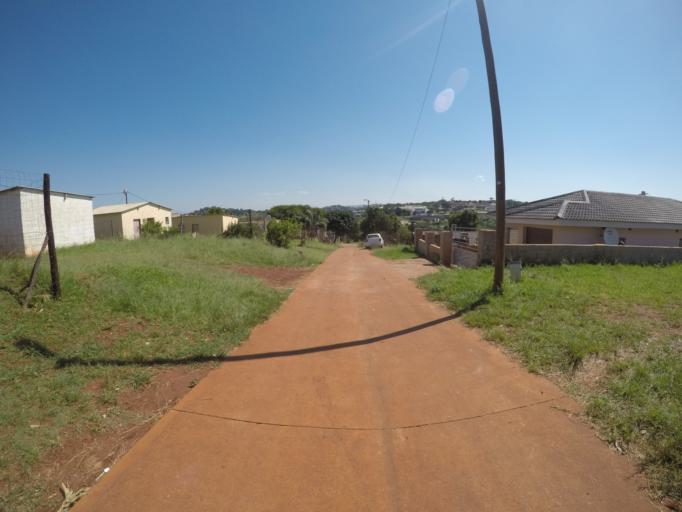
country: ZA
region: KwaZulu-Natal
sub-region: uThungulu District Municipality
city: Empangeni
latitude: -28.7744
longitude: 31.8778
